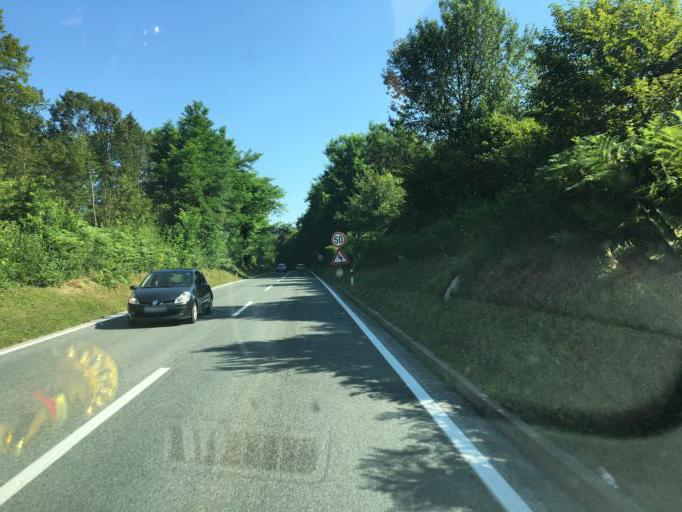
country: HR
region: Karlovacka
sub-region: Grad Karlovac
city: Slunj
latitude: 45.1710
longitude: 15.5613
